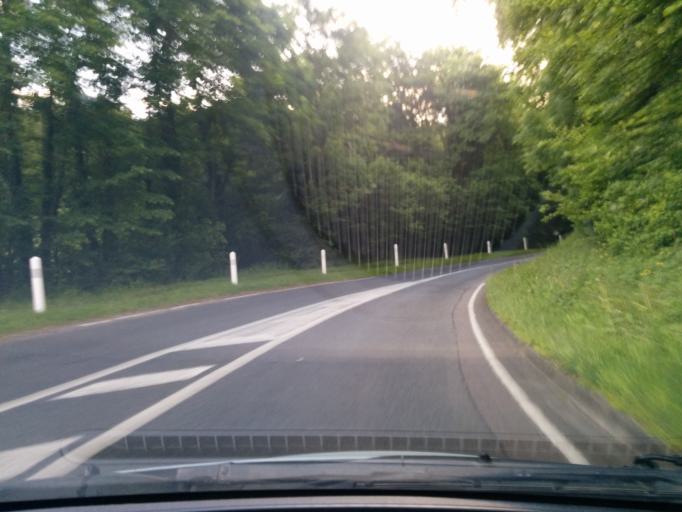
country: FR
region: Haute-Normandie
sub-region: Departement de l'Eure
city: Vernon
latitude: 49.0995
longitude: 1.5034
